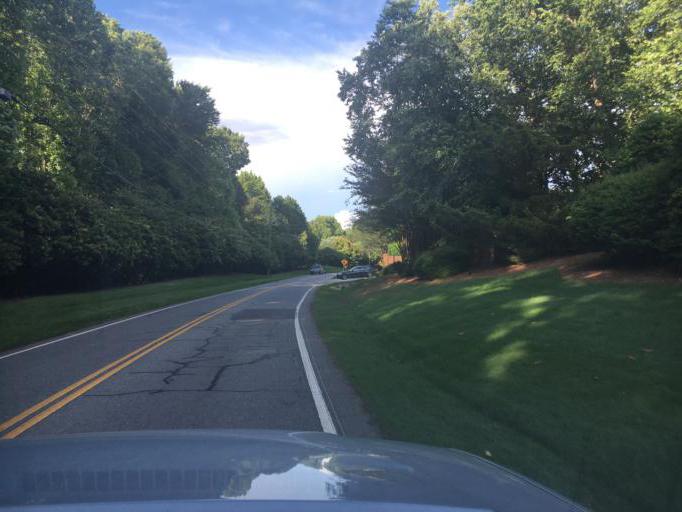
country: US
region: South Carolina
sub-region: Greenville County
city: Five Forks
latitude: 34.7894
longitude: -82.2368
